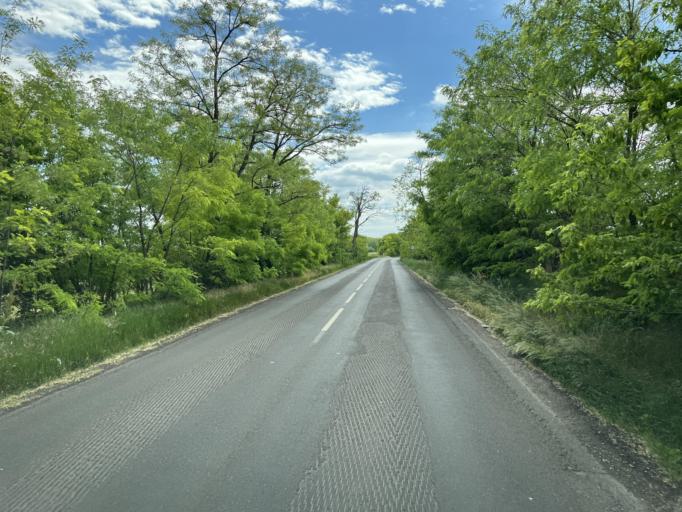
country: HU
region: Pest
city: Szentlorinckata
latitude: 47.4937
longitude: 19.7369
